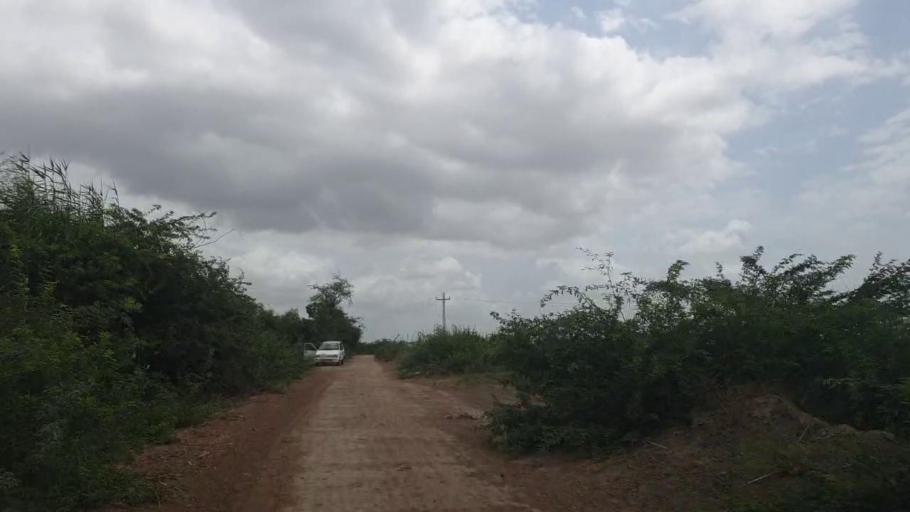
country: PK
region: Sindh
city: Badin
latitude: 24.6330
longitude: 68.9479
